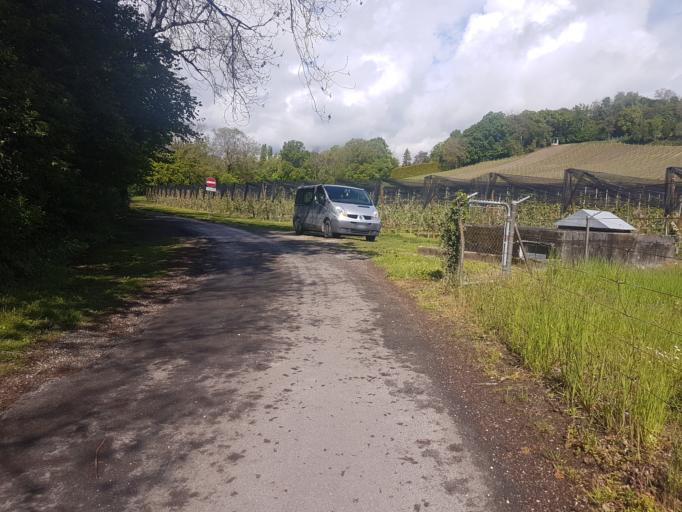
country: CH
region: Vaud
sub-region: Nyon District
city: Perroy
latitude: 46.4657
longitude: 6.3818
